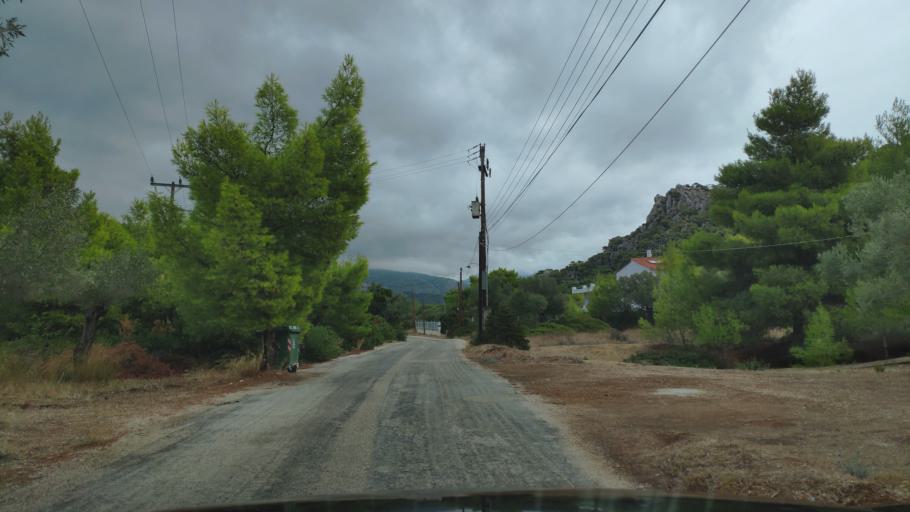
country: GR
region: Peloponnese
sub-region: Nomos Korinthias
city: Perachora
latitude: 38.0309
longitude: 22.8627
